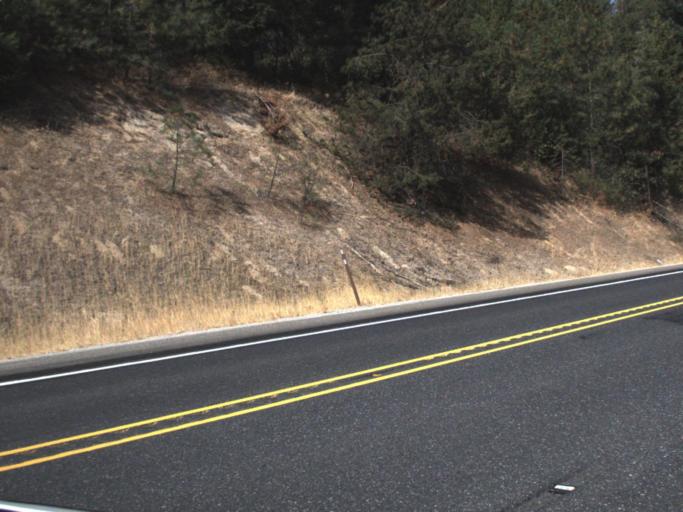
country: US
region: Washington
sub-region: Spokane County
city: Deer Park
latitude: 48.0221
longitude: -117.5922
